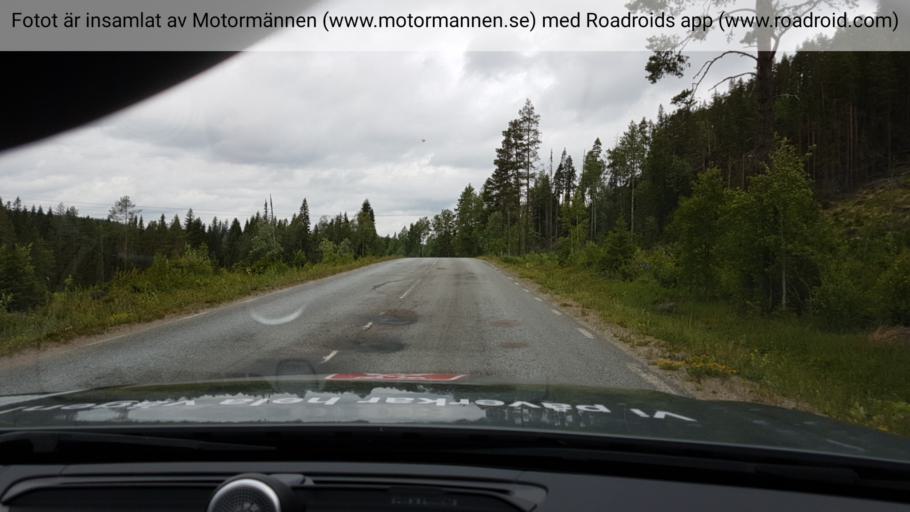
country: SE
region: Jaemtland
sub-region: Braecke Kommun
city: Braecke
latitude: 62.7943
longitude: 15.4729
